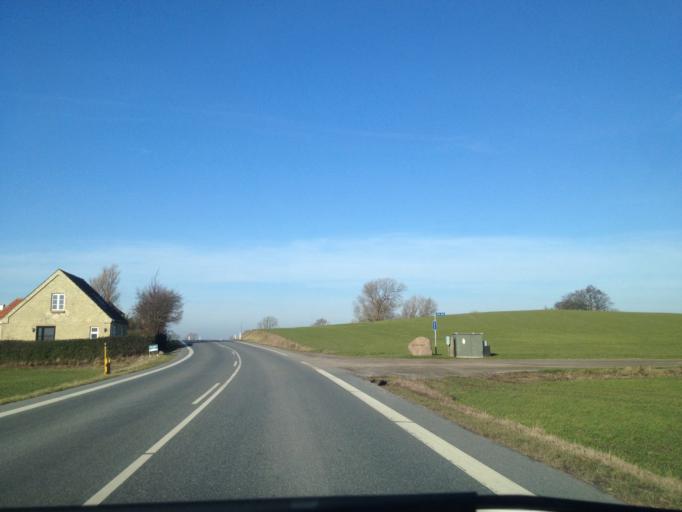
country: DK
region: South Denmark
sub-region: Kerteminde Kommune
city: Kerteminde
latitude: 55.4810
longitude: 10.6615
